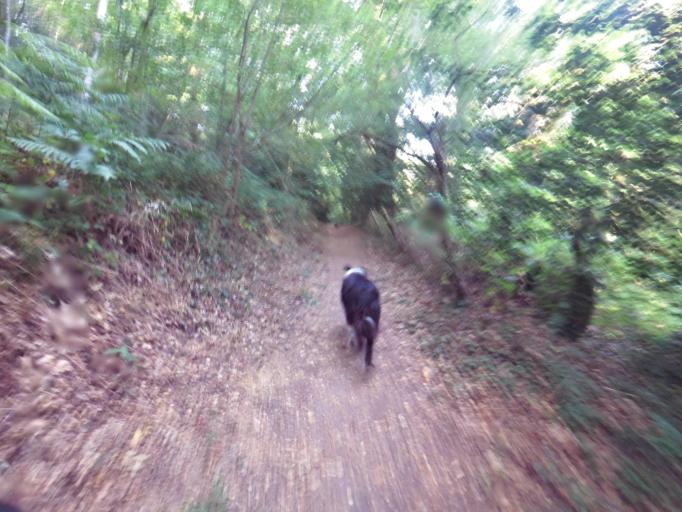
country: FR
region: Brittany
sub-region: Departement du Morbihan
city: Pluherlin
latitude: 47.7029
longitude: -2.3447
